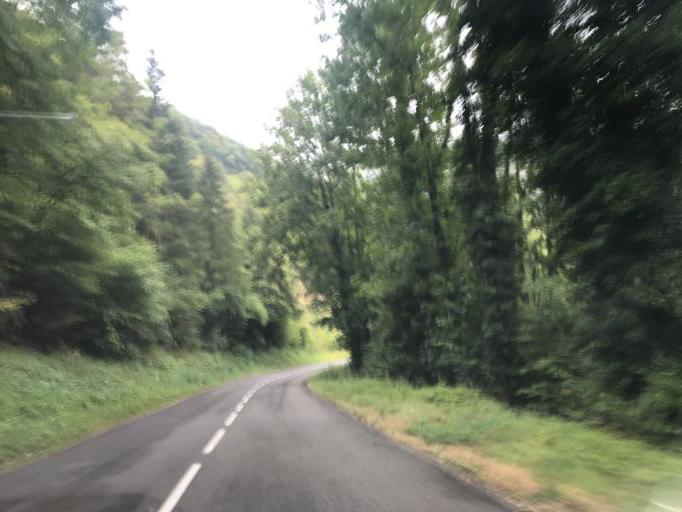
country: FR
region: Rhone-Alpes
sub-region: Departement de l'Ain
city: Dortan
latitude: 46.3231
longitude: 5.6481
